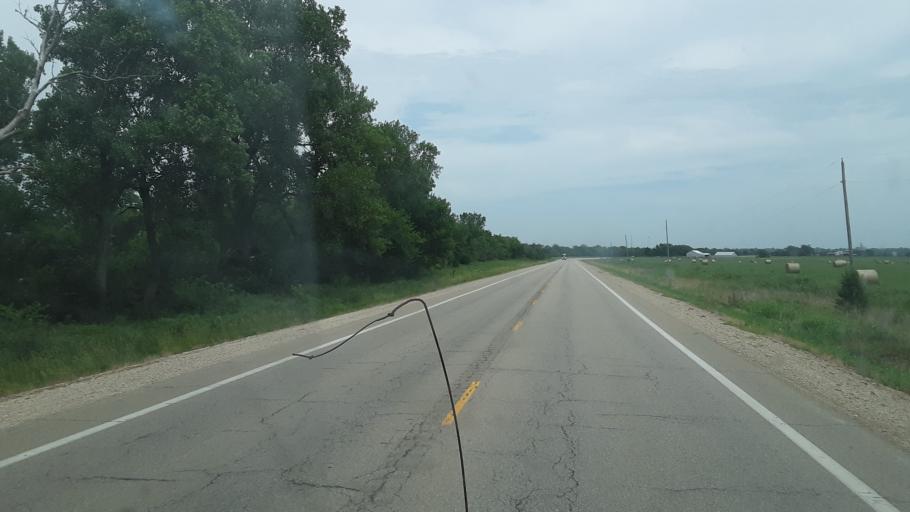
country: US
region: Kansas
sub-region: Woodson County
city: Yates Center
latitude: 37.8766
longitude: -95.7755
